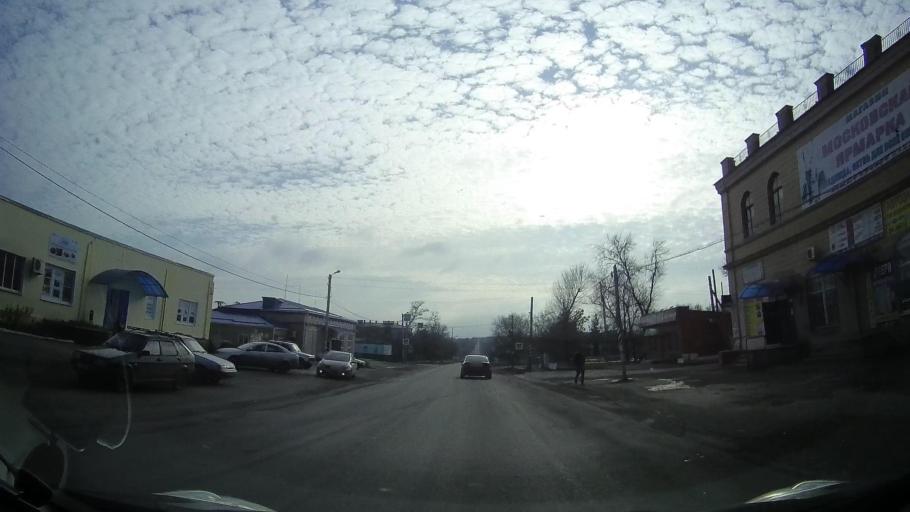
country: RU
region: Rostov
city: Mechetinskaya
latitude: 46.7672
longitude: 40.4549
